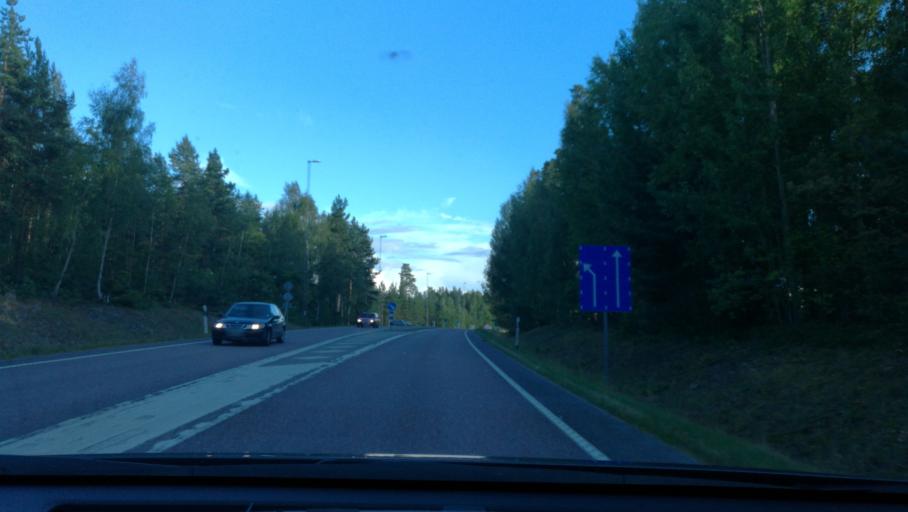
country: SE
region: Vaestmanland
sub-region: Kungsors Kommun
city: Kungsoer
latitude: 59.2806
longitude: 16.1192
